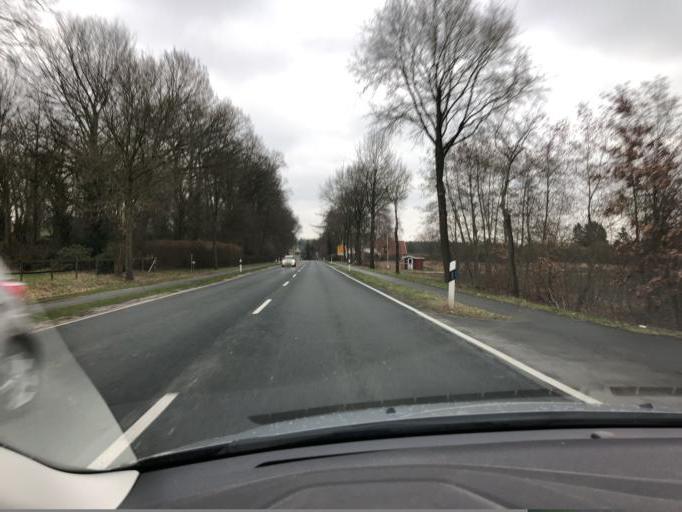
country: DE
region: Lower Saxony
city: Wiefelstede
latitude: 53.1705
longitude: 8.1348
